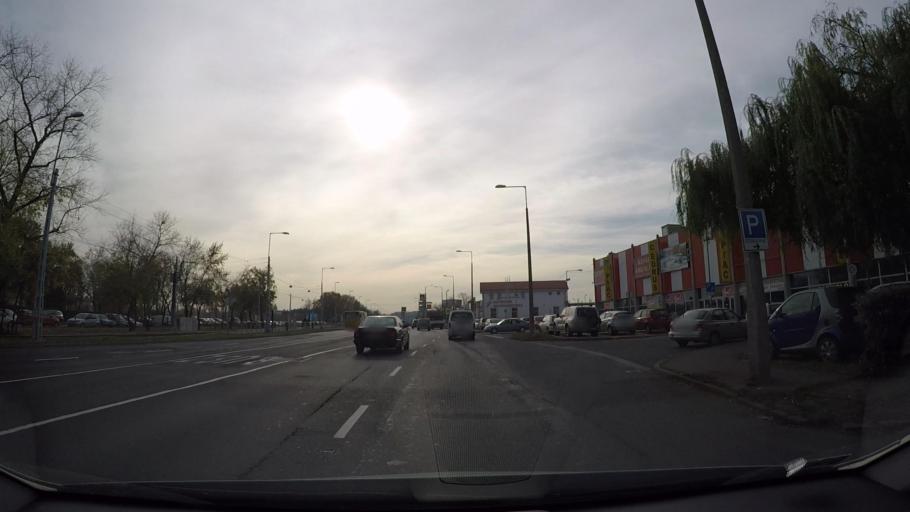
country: HU
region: Budapest
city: Budapest X. keruelet
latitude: 47.5006
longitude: 19.1370
